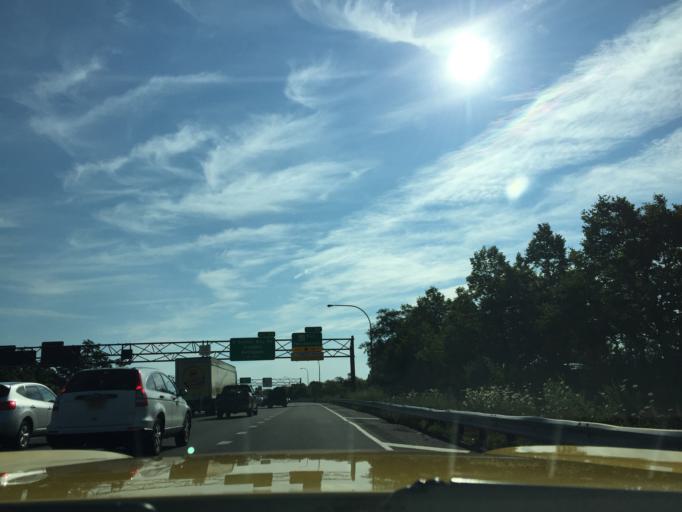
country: US
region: New York
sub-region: Nassau County
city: Jericho
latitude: 40.7861
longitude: -73.5292
